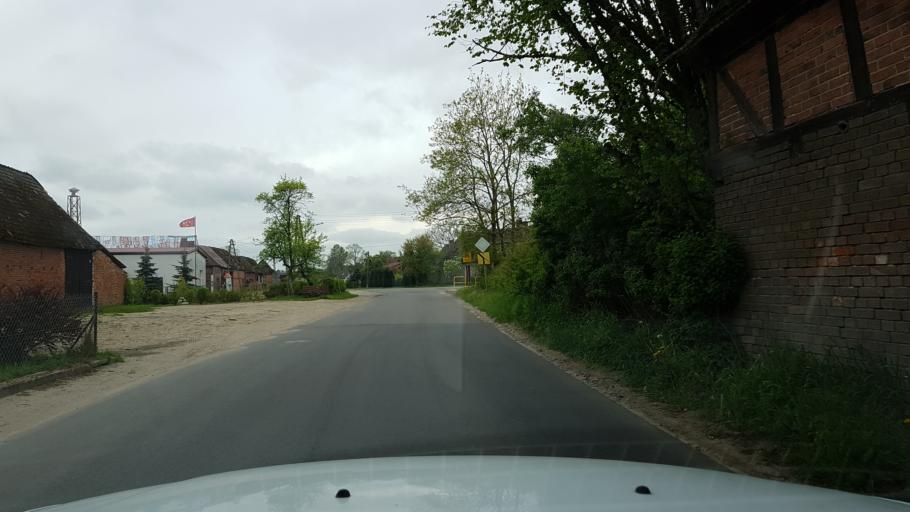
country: PL
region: West Pomeranian Voivodeship
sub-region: Powiat slawienski
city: Slawno
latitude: 54.3931
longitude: 16.7064
